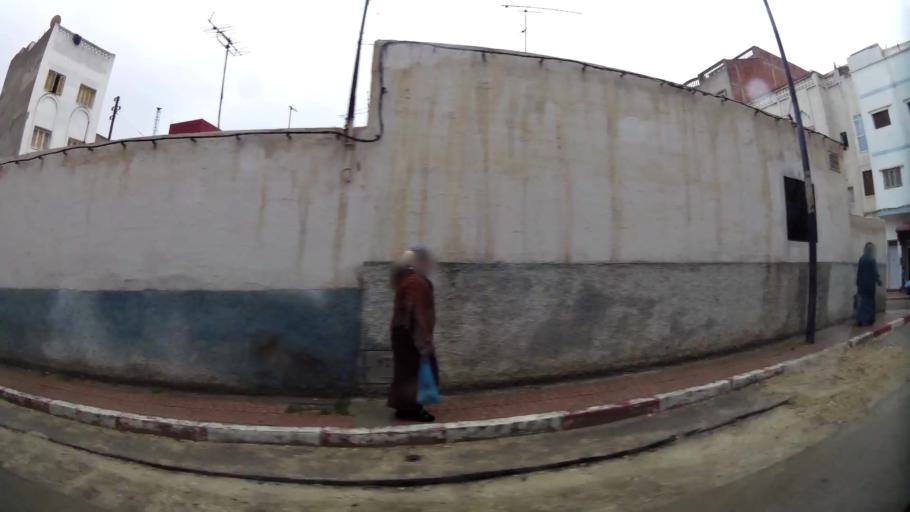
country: MA
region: Taza-Al Hoceima-Taounate
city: Al Hoceima
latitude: 35.2505
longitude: -3.9346
